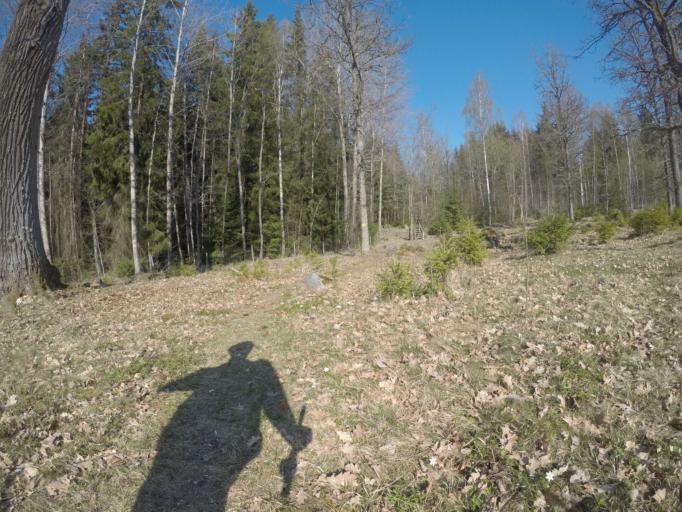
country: SE
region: Vaestmanland
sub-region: Hallstahammars Kommun
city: Kolback
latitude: 59.5349
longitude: 16.2814
